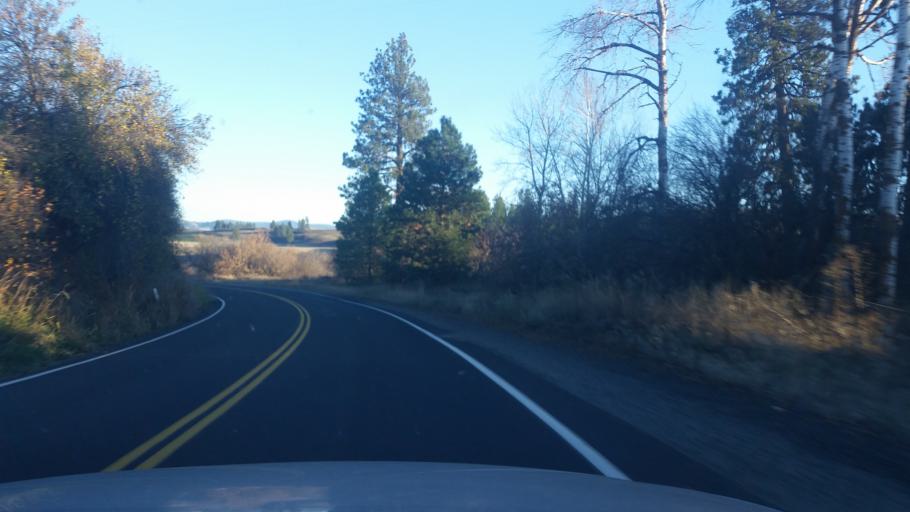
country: US
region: Washington
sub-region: Spokane County
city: Opportunity
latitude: 47.3530
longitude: -117.2632
